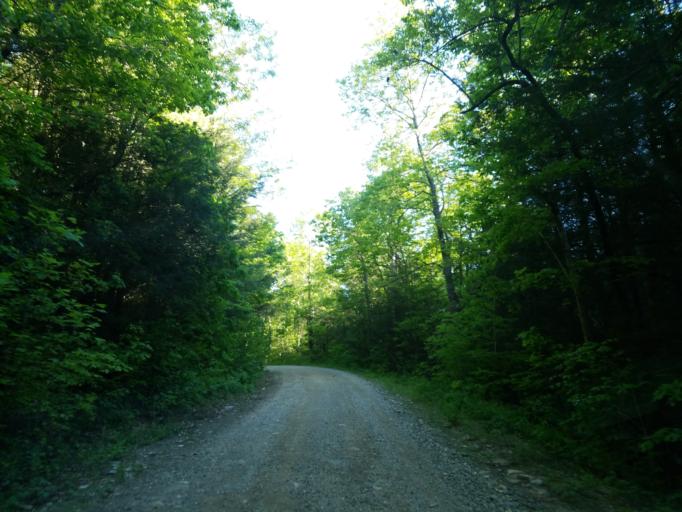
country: US
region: Georgia
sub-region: Lumpkin County
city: Dahlonega
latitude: 34.6706
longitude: -84.1305
